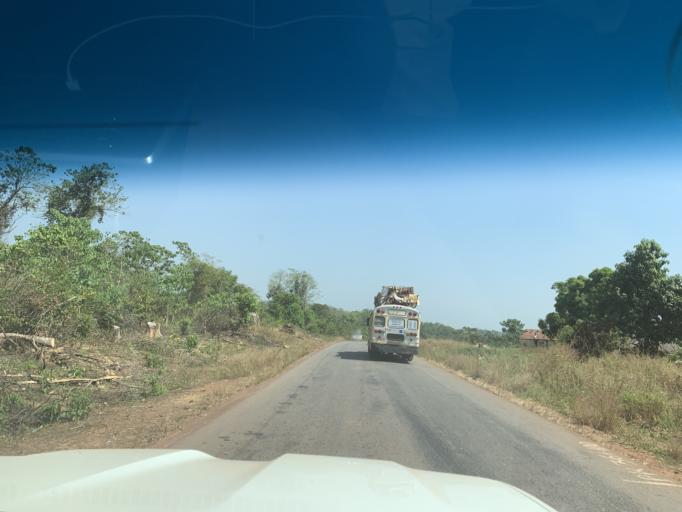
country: GN
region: Kindia
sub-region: Kindia
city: Kindia
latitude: 10.0044
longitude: -12.7028
